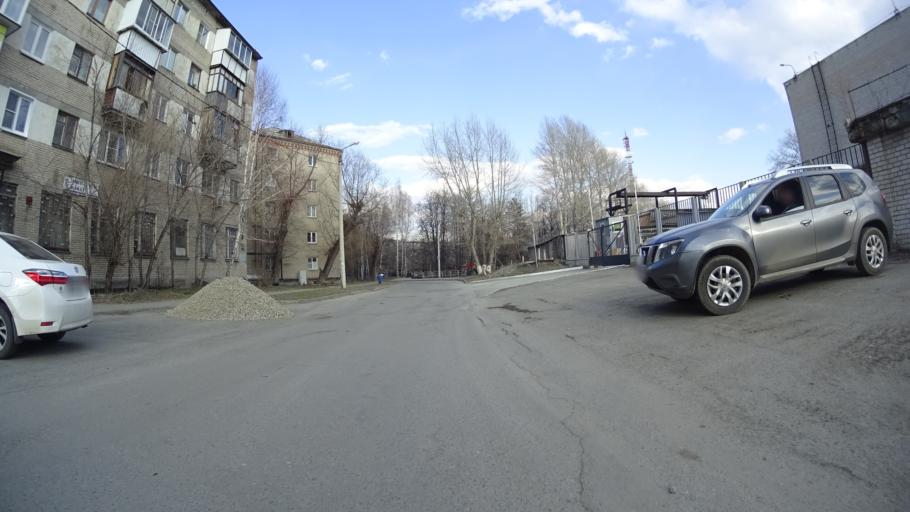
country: RU
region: Chelyabinsk
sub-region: Gorod Chelyabinsk
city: Chelyabinsk
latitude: 55.1438
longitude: 61.3732
